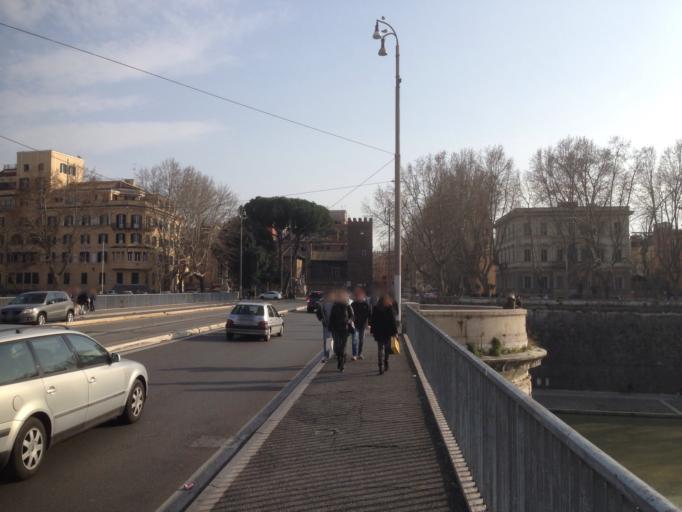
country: VA
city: Vatican City
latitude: 41.8913
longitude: 12.4744
